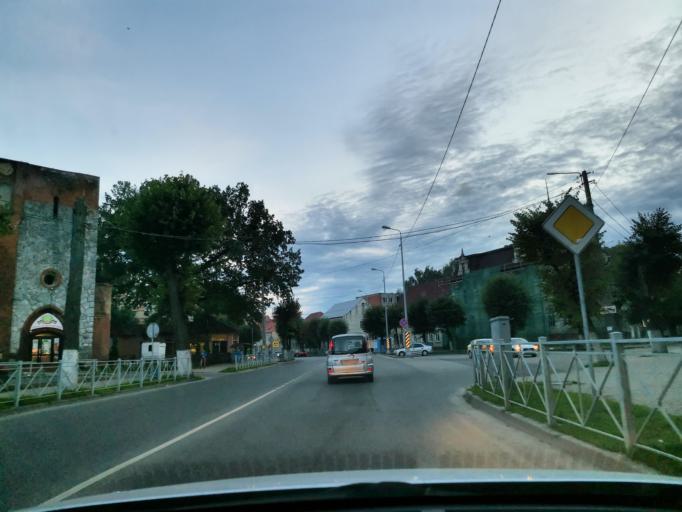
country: RU
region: Kaliningrad
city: Sovetsk
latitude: 55.0786
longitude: 21.8861
